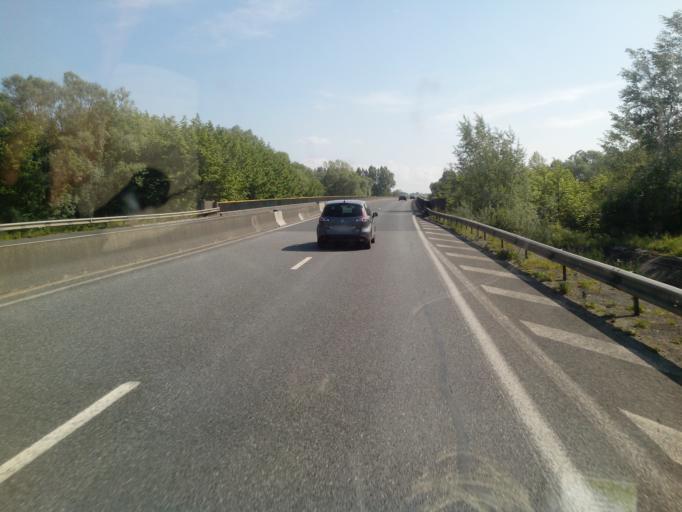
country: FR
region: Picardie
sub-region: Departement de la Somme
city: Abbeville
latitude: 50.1205
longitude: 1.7954
